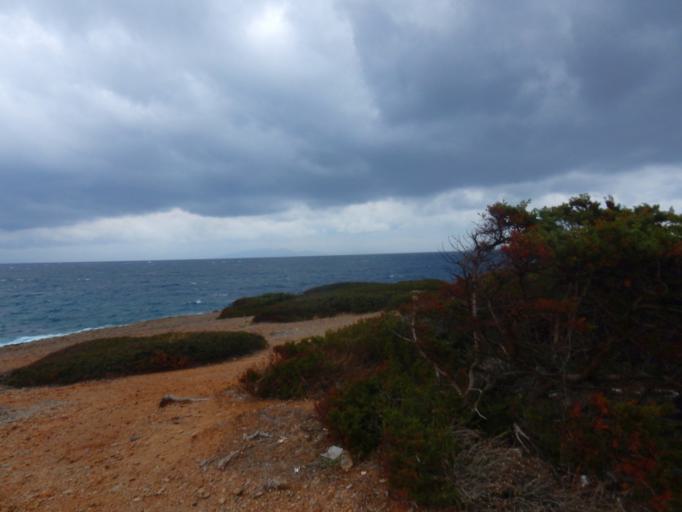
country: GR
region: Attica
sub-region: Nomarchia Anatolikis Attikis
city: Limin Mesoyaias
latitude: 37.9099
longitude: 24.0395
